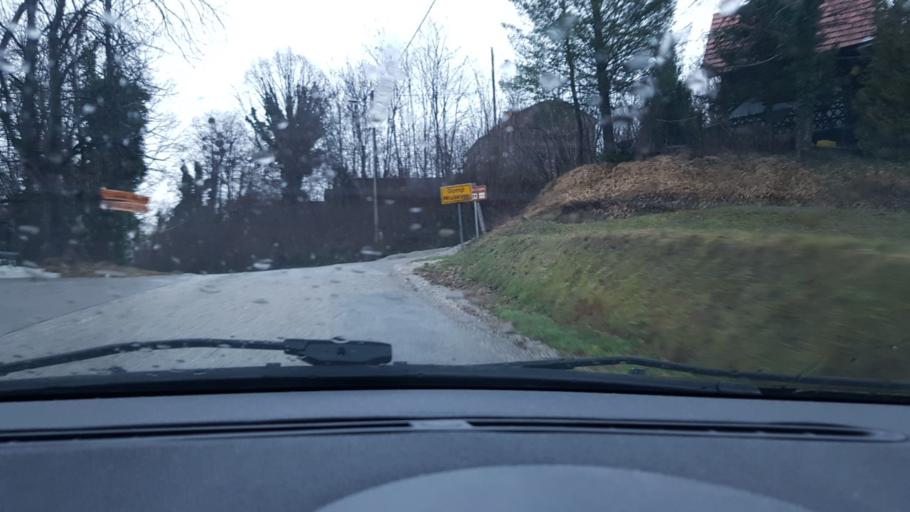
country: HR
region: Krapinsko-Zagorska
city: Bedekovcina
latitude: 45.9952
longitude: 15.9827
